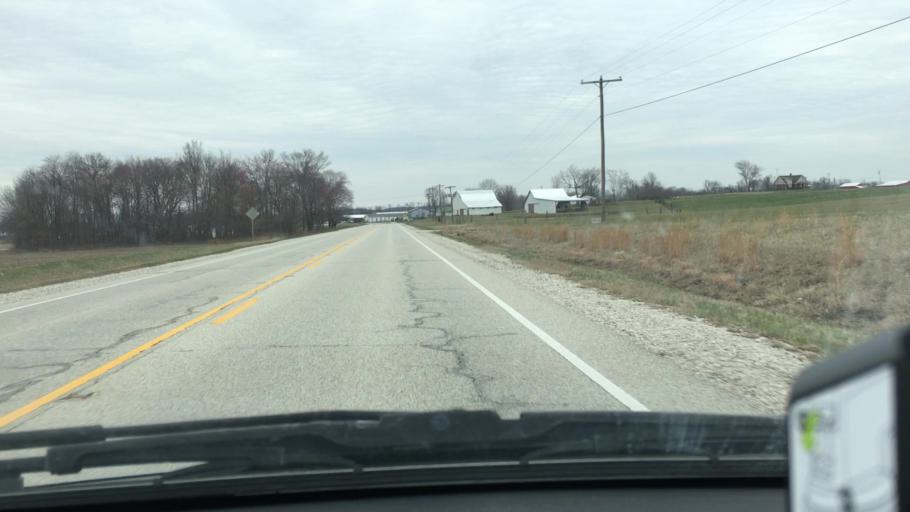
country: US
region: Indiana
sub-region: Greene County
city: Bloomfield
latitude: 39.0211
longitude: -87.0146
